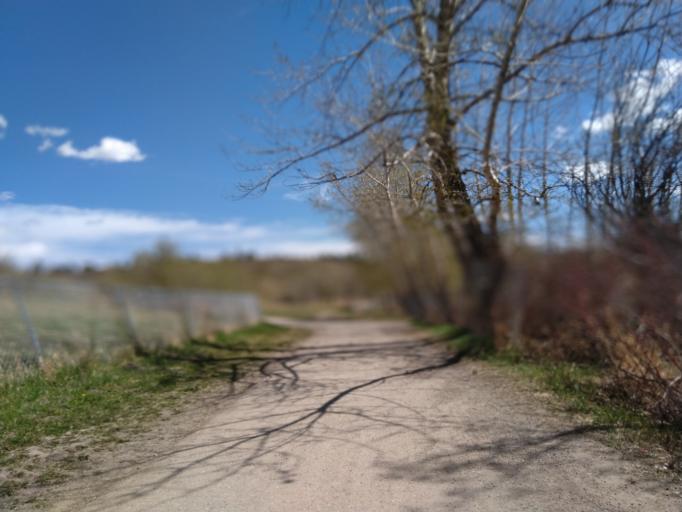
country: CA
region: Alberta
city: Calgary
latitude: 51.0997
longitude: -114.2021
